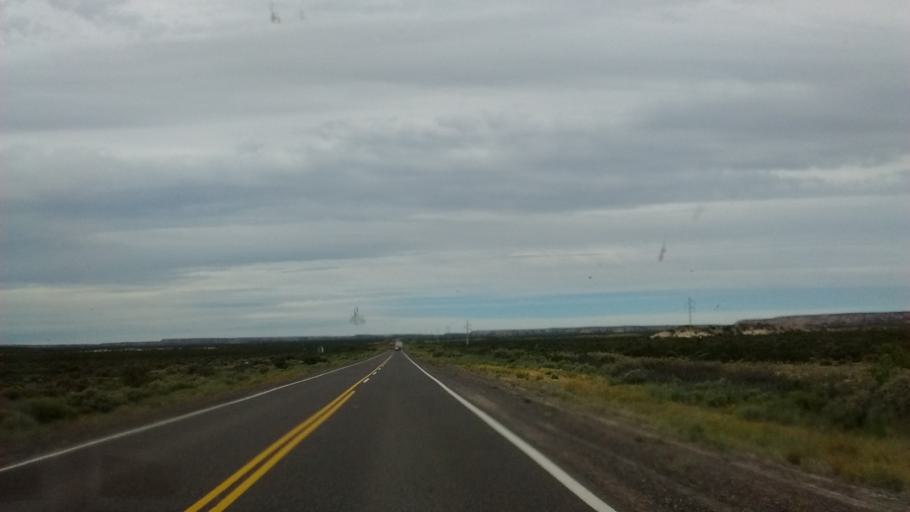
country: AR
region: Rio Negro
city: Catriel
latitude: -38.1303
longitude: -67.9344
